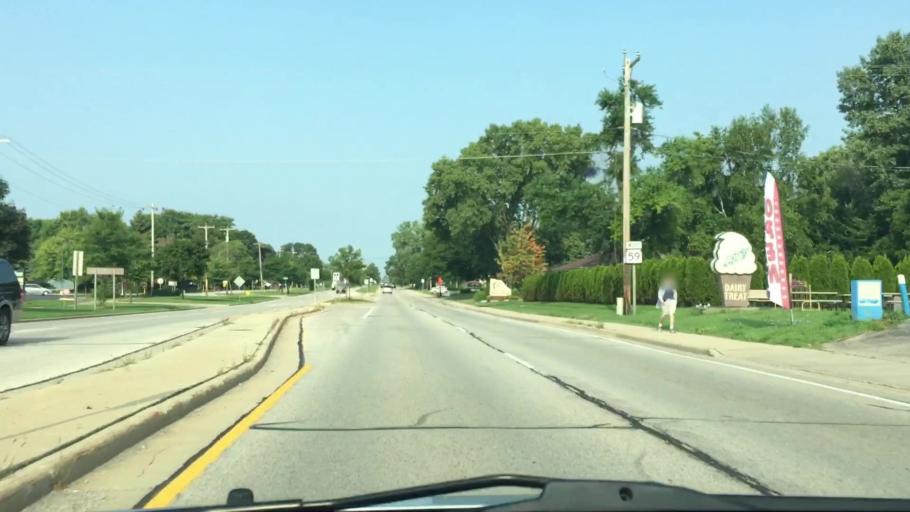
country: US
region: Wisconsin
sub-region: Waukesha County
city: Elm Grove
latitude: 43.0167
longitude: -88.0880
